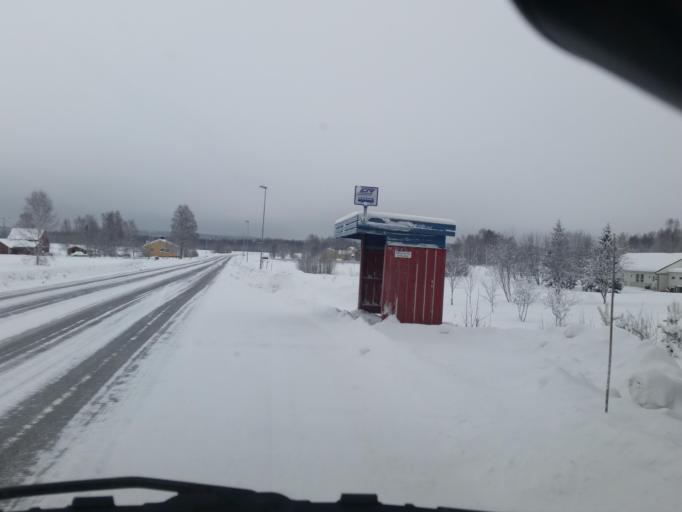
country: SE
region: Norrbotten
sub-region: Pitea Kommun
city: Roknas
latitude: 65.4419
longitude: 21.2646
